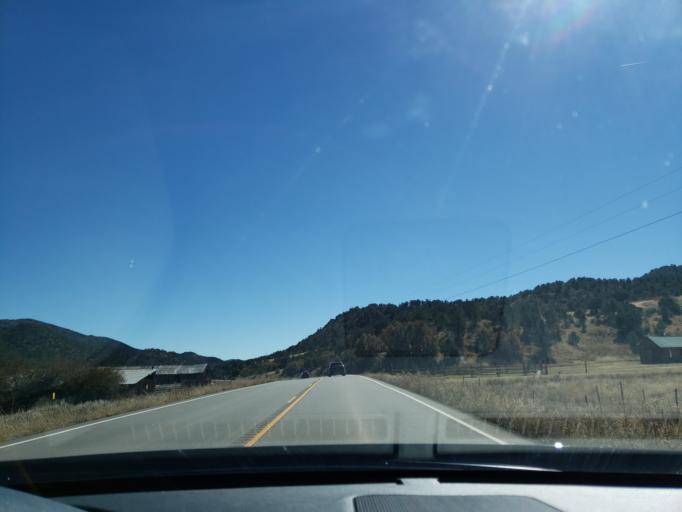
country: US
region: Colorado
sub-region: Fremont County
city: Canon City
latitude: 38.6056
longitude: -105.4363
